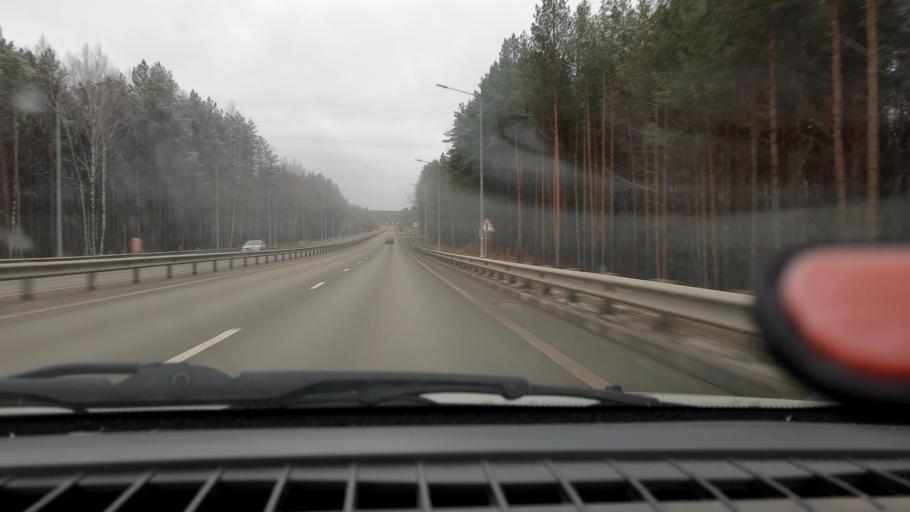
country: RU
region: Nizjnij Novgorod
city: Burevestnik
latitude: 56.0925
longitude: 43.9196
